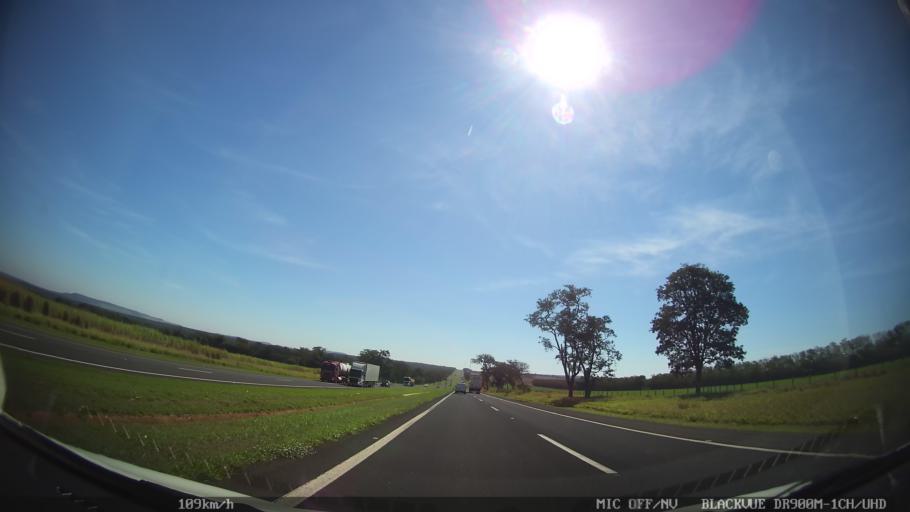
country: BR
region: Sao Paulo
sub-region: Santa Rita Do Passa Quatro
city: Santa Rita do Passa Quatro
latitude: -21.6452
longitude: -47.6111
